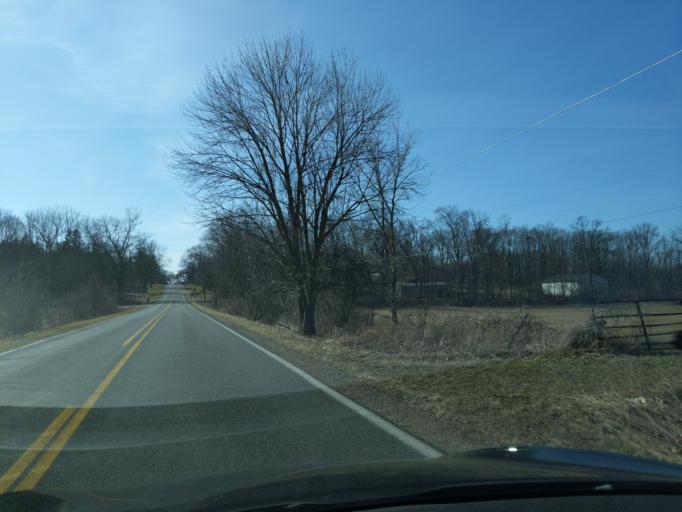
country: US
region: Michigan
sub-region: Ionia County
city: Saranac
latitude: 42.9296
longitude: -85.1868
